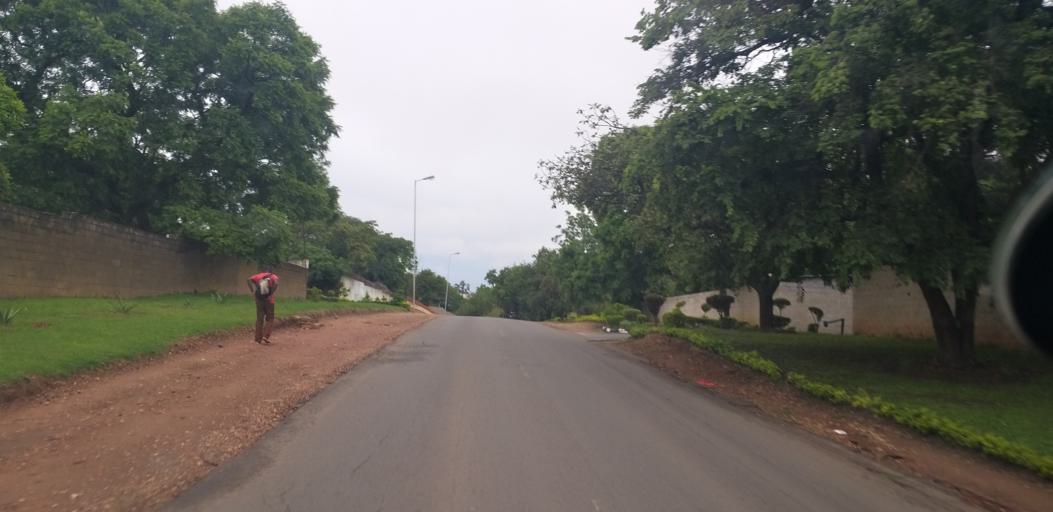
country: ZM
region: Lusaka
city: Lusaka
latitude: -15.4261
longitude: 28.3350
